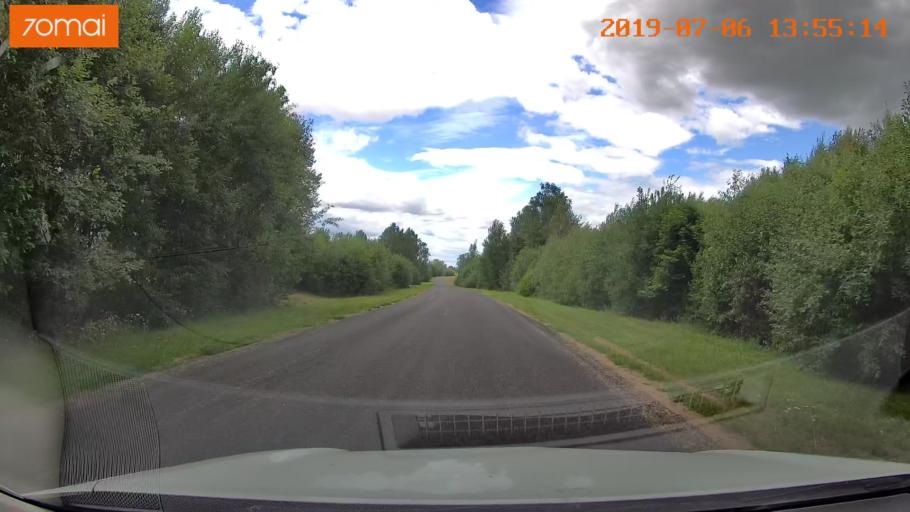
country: BY
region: Minsk
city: Ivyanyets
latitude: 53.7536
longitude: 26.8107
